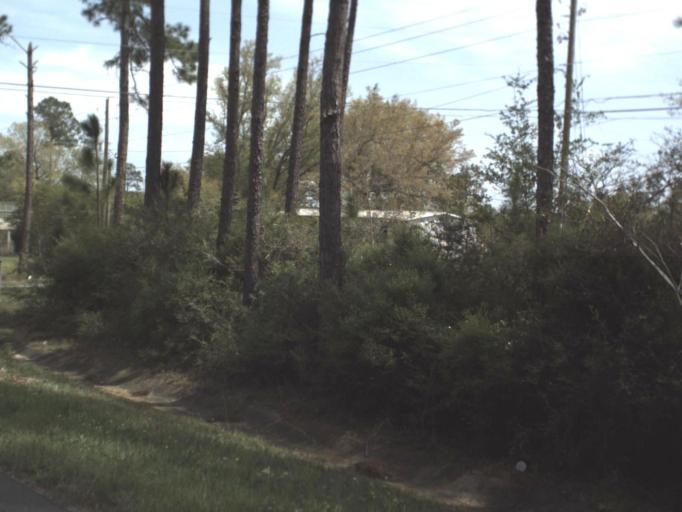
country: US
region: Florida
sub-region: Escambia County
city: Gonzalez
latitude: 30.5349
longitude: -87.3472
